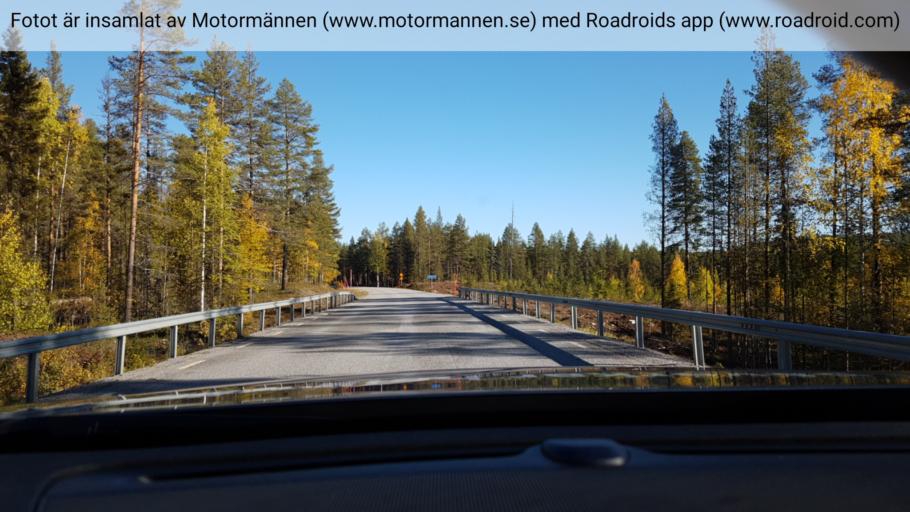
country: SE
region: Norrbotten
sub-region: Gallivare Kommun
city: Gaellivare
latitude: 66.4735
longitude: 20.8571
